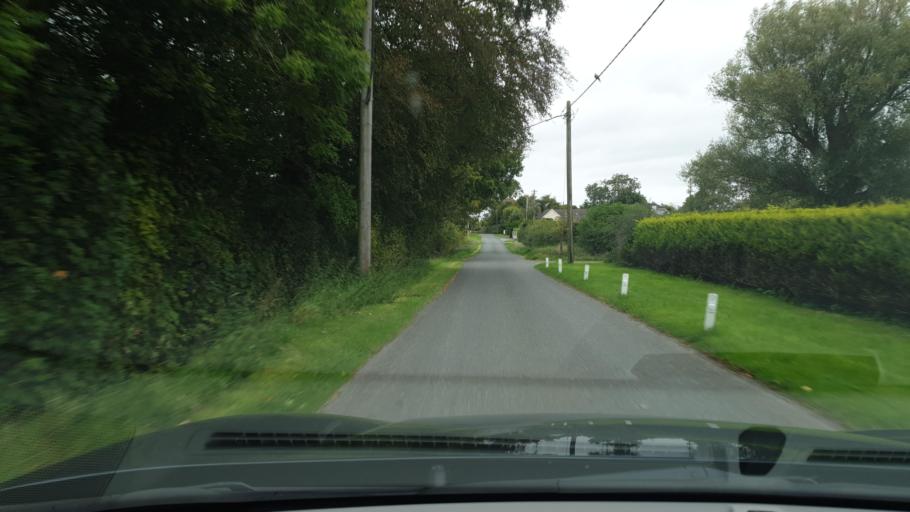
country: IE
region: Leinster
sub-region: An Mhi
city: Ratoath
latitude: 53.4969
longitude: -6.4902
